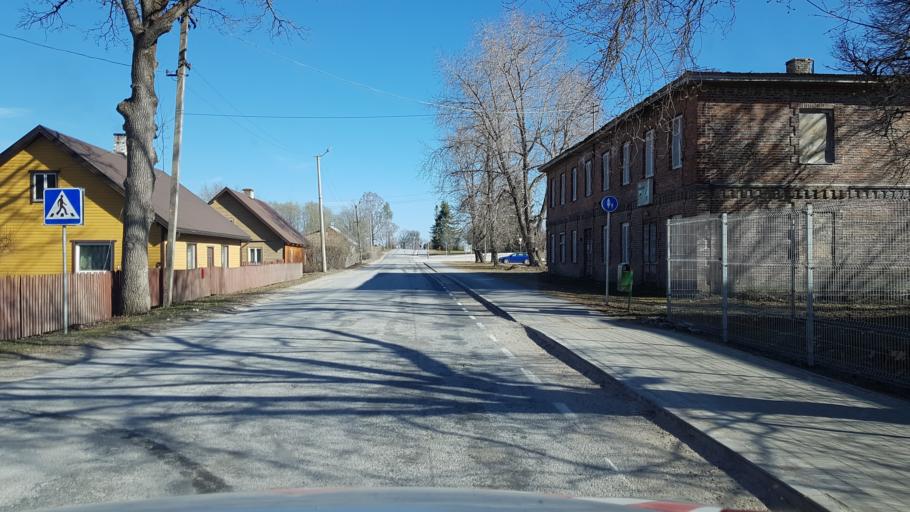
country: EE
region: Laeaene-Virumaa
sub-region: Rakke vald
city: Rakke
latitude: 58.9869
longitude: 26.2458
